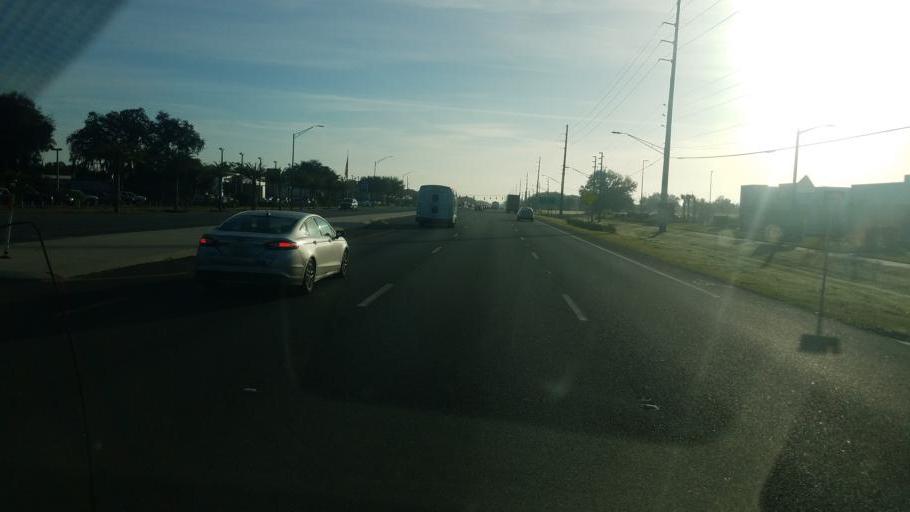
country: US
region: Florida
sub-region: Osceola County
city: Saint Cloud
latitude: 28.2460
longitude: -81.2599
